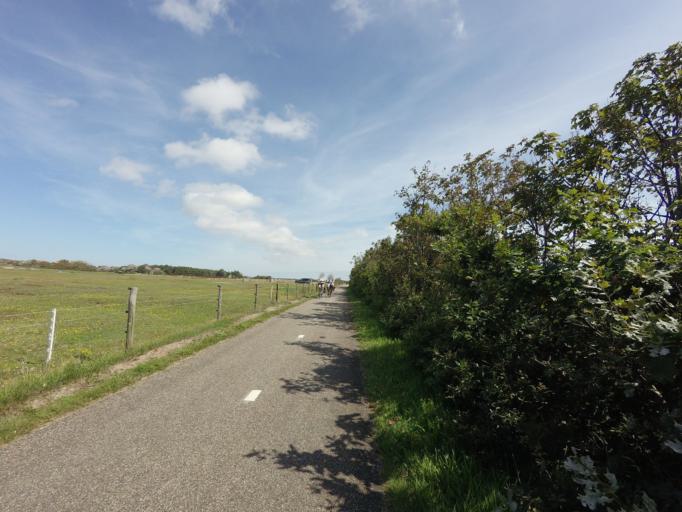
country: NL
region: Friesland
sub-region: Gemeente Ameland
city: Hollum
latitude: 53.4457
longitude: 5.6560
